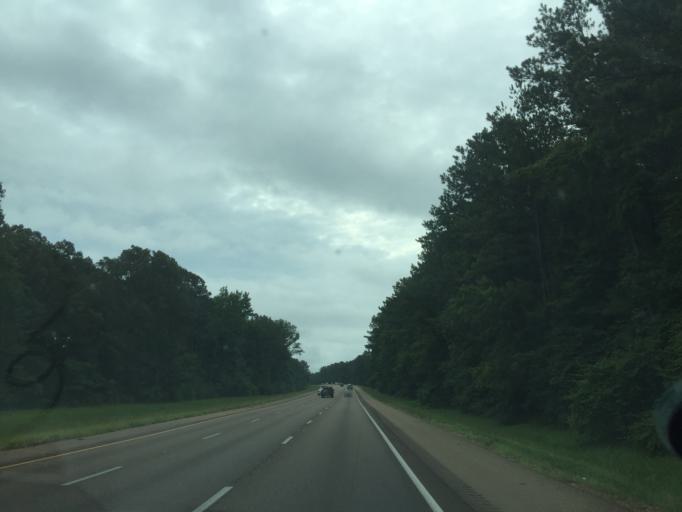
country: US
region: Mississippi
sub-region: Rankin County
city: Pearl
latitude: 32.2659
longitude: -90.1120
